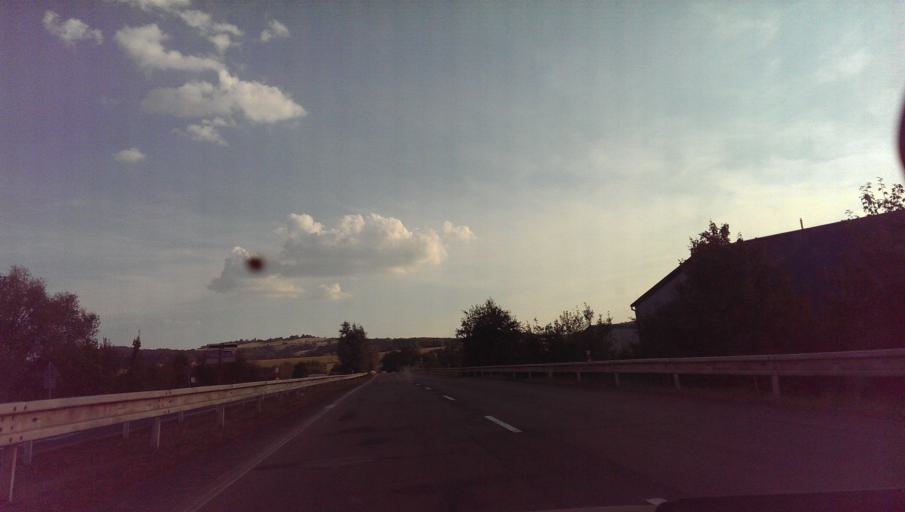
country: CZ
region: Zlin
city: Slusovice
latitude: 49.2162
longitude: 17.7797
